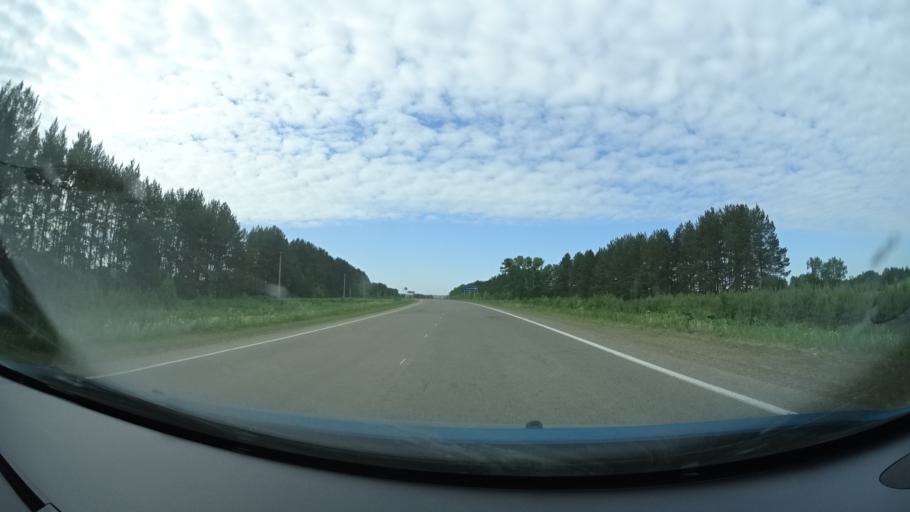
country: RU
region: Perm
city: Kuyeda
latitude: 56.4800
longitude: 55.5913
